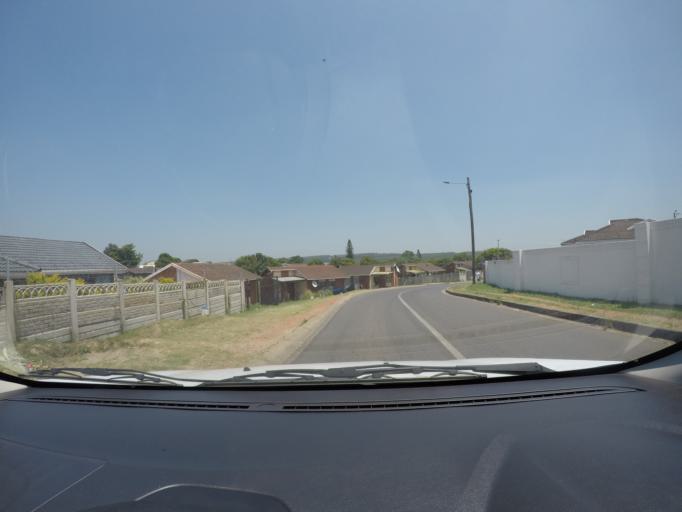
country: ZA
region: KwaZulu-Natal
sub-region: uThungulu District Municipality
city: eSikhawini
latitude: -28.8716
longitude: 31.9109
